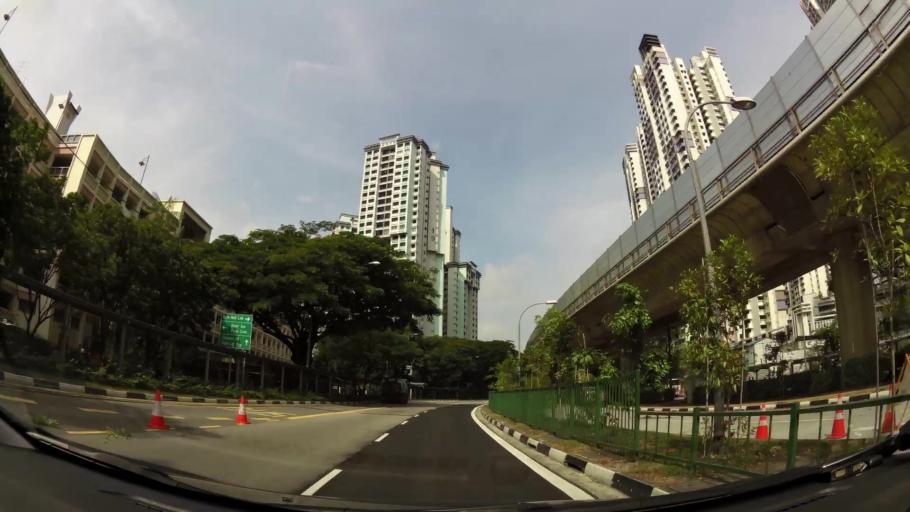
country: SG
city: Singapore
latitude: 1.3076
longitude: 103.7851
